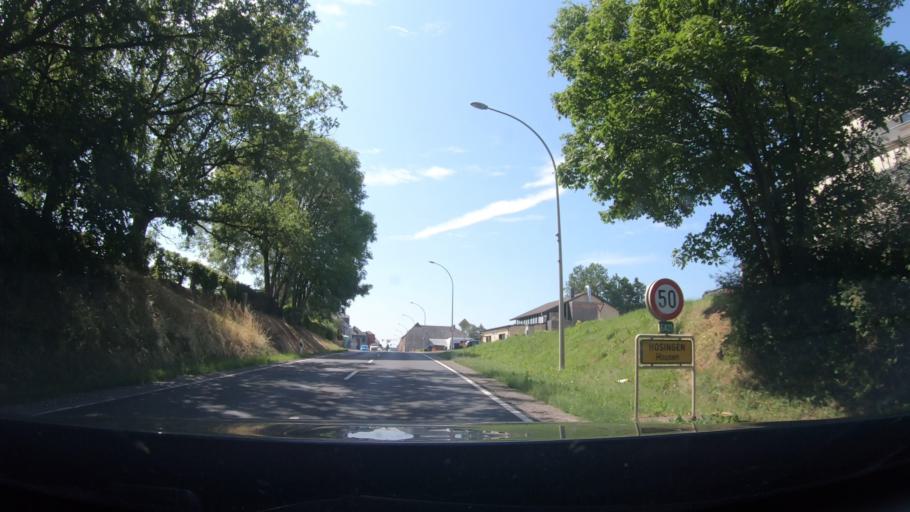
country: LU
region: Diekirch
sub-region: Canton de Clervaux
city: Hosingen
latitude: 50.0206
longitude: 6.0918
